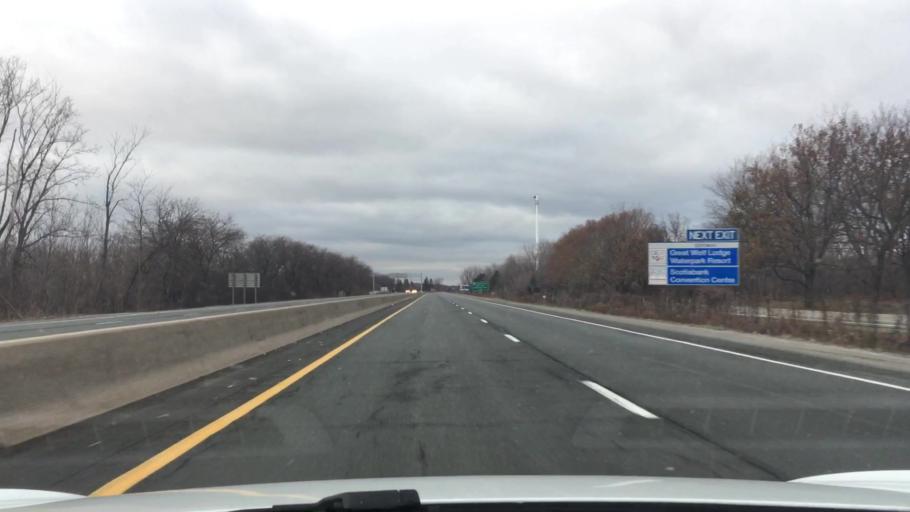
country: US
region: New York
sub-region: Niagara County
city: Lewiston
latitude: 43.1522
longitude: -79.0765
